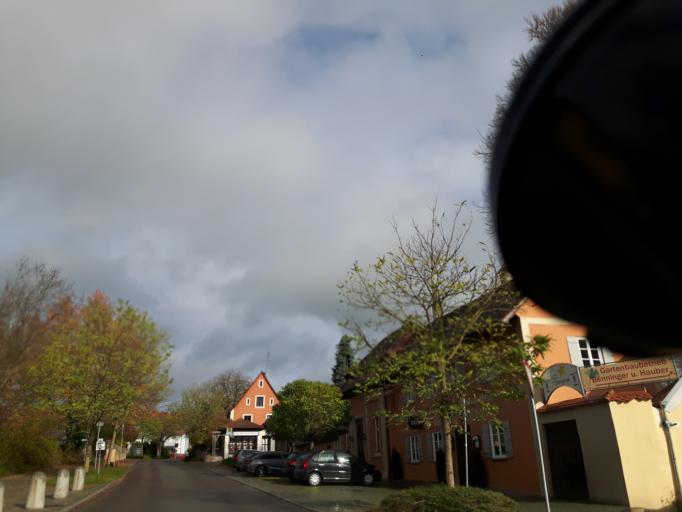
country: DE
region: Bavaria
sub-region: Regierungsbezirk Mittelfranken
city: Dinkelsbuhl
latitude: 49.0726
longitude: 10.3193
